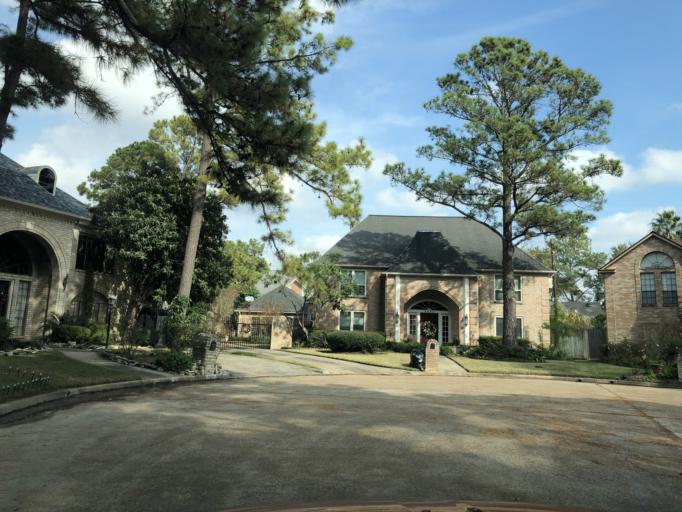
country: US
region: Texas
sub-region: Harris County
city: Tomball
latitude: 30.0242
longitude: -95.5426
